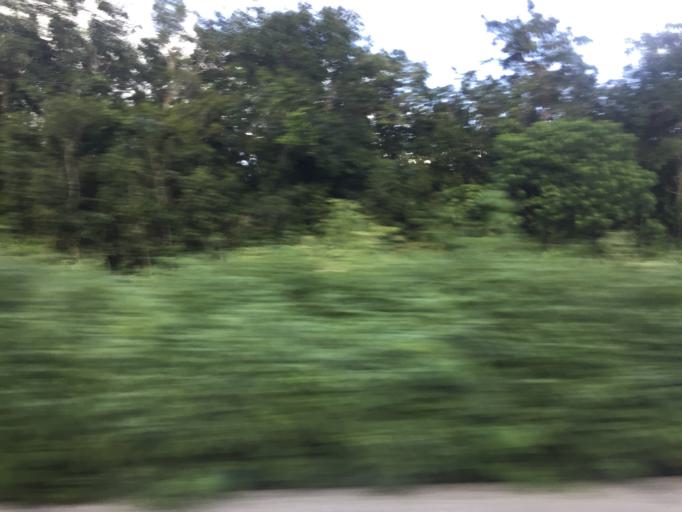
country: MX
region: Quintana Roo
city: Tulum
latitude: 20.2681
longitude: -87.4795
